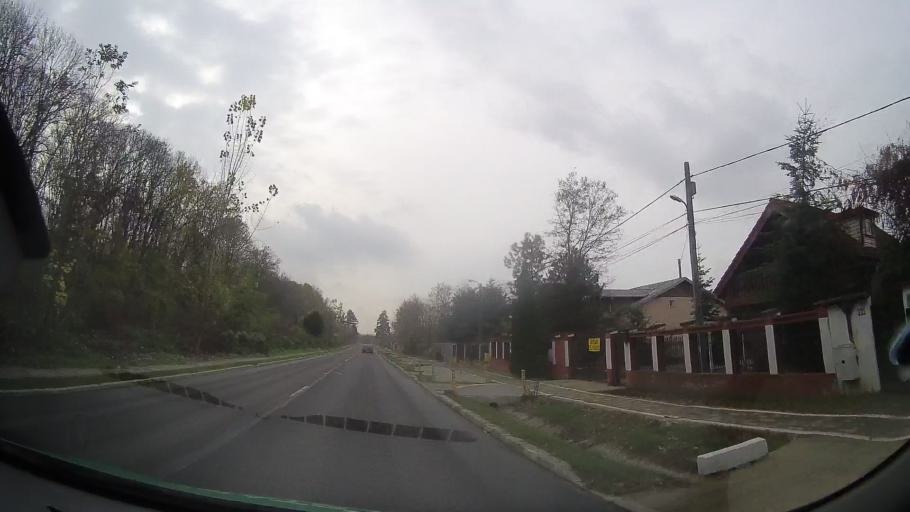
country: RO
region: Ilfov
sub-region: Comuna Snagov
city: Snagov
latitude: 44.7133
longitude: 26.1914
